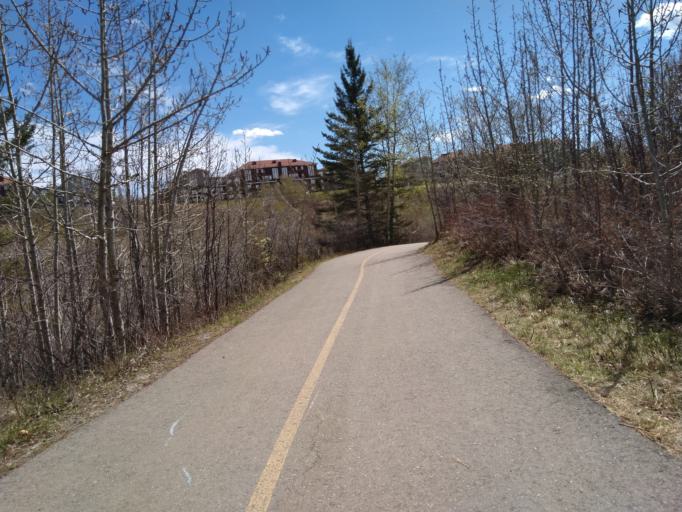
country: CA
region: Alberta
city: Calgary
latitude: 51.1241
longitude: -114.2384
